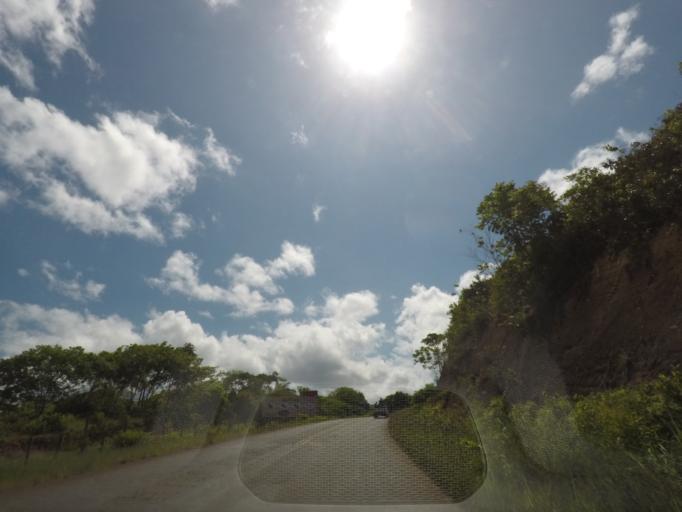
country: BR
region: Bahia
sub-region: Taperoa
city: Taperoa
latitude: -13.5170
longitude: -39.0974
